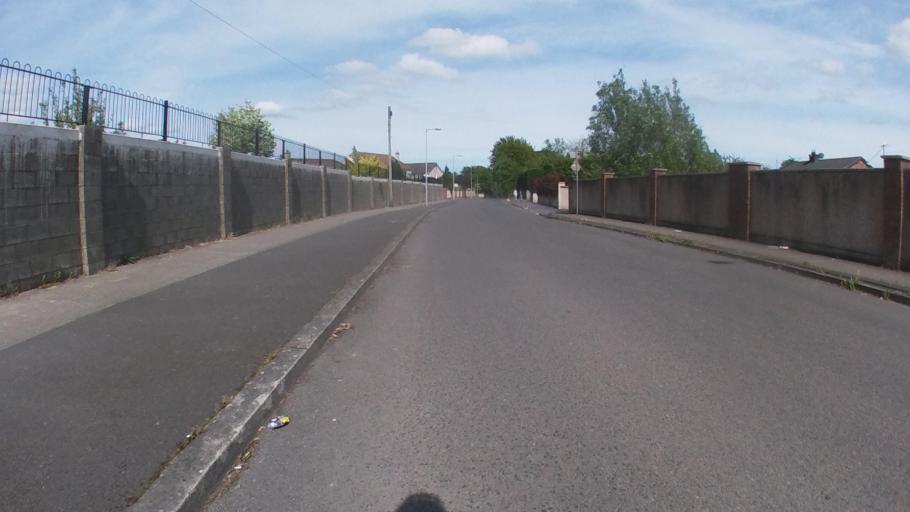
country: IE
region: Leinster
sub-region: County Carlow
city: Carlow
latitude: 52.8345
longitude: -6.9455
